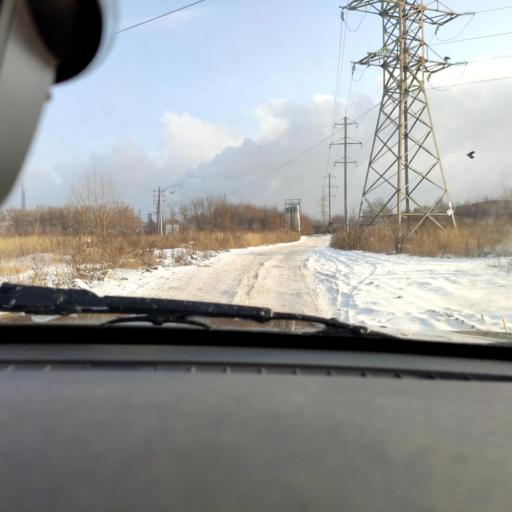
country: RU
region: Samara
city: Tol'yatti
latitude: 53.5465
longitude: 49.4283
